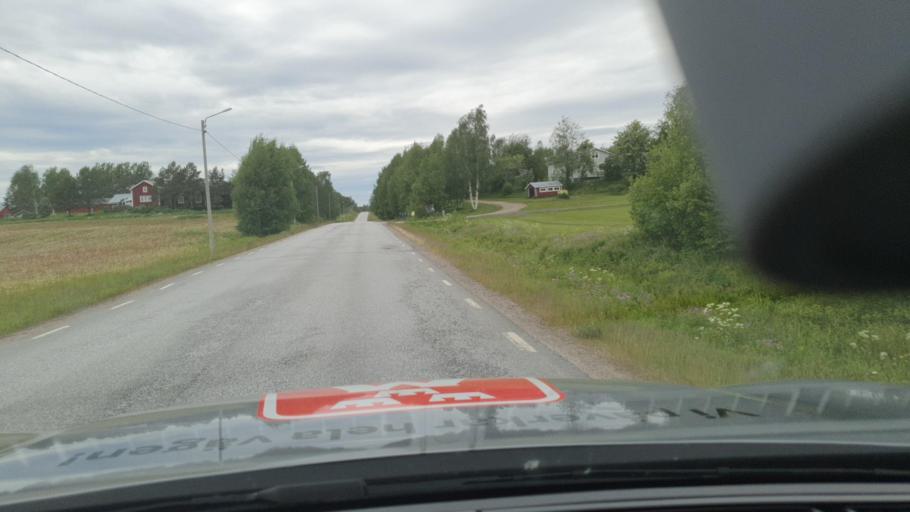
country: SE
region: Norrbotten
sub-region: Kalix Kommun
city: Rolfs
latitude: 65.8842
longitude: 22.9907
